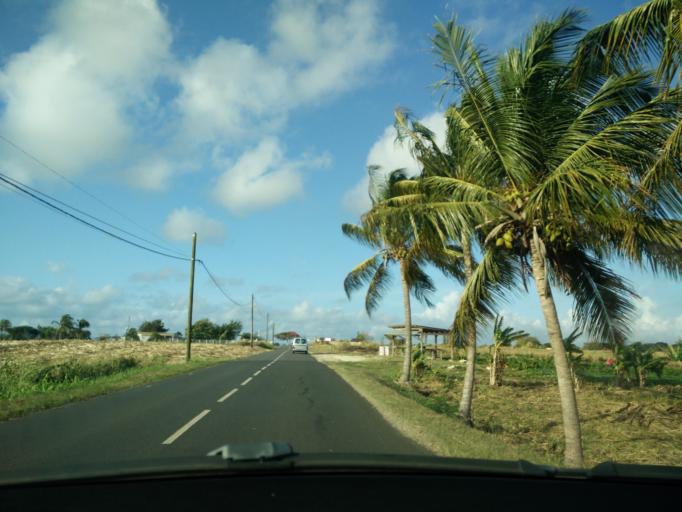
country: GP
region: Guadeloupe
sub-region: Guadeloupe
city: Le Moule
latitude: 16.3091
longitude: -61.3669
